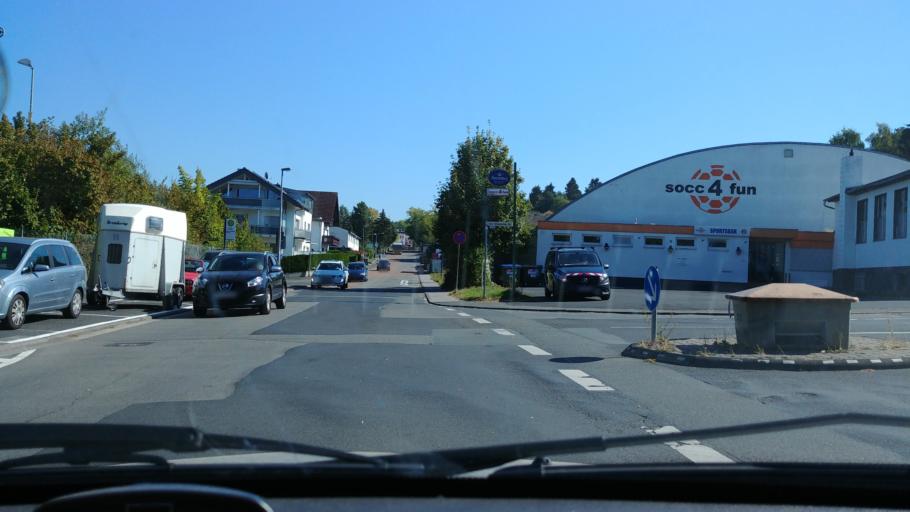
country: DE
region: Hesse
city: Taunusstein
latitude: 50.1370
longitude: 8.1493
